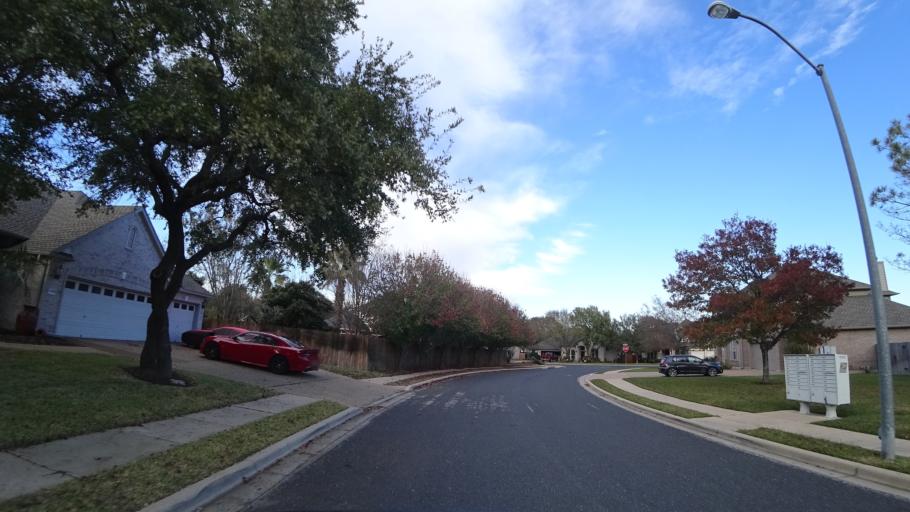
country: US
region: Texas
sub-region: Williamson County
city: Brushy Creek
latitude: 30.5031
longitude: -97.7391
